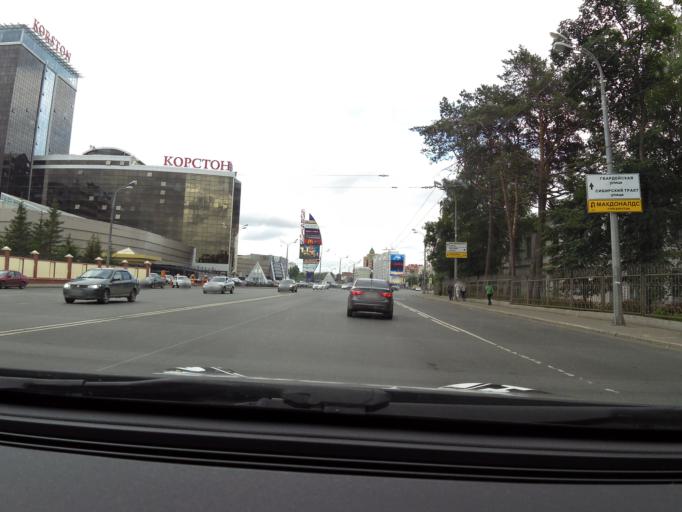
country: RU
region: Tatarstan
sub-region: Gorod Kazan'
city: Kazan
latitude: 55.7936
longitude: 49.1467
